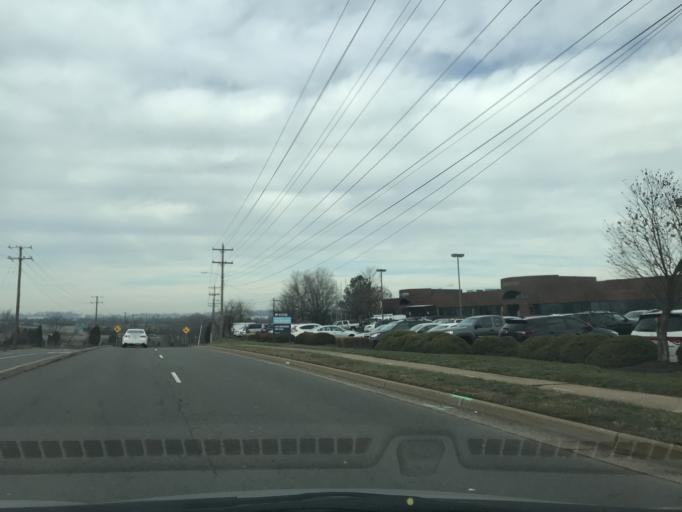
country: US
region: Virginia
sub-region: City of Manassas
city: Manassas
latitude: 38.7418
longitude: -77.5098
